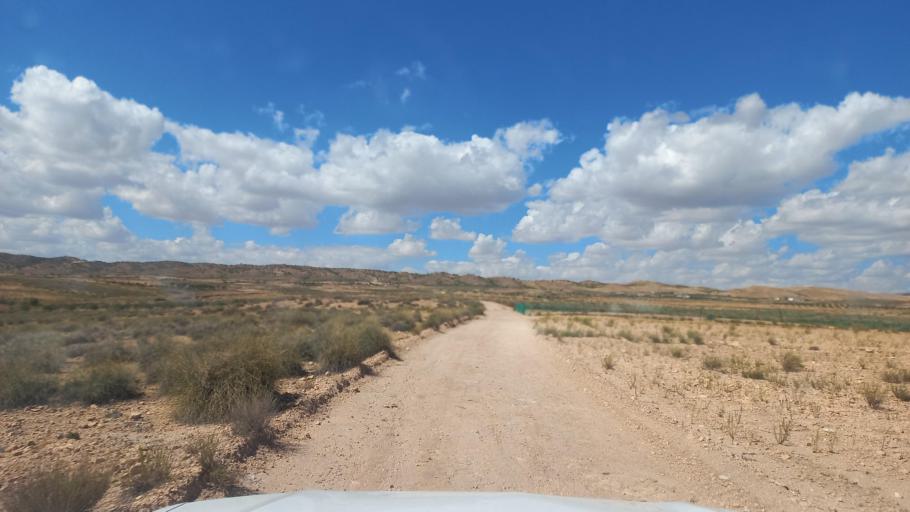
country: TN
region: Al Qasrayn
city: Sbiba
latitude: 35.3557
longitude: 9.0108
